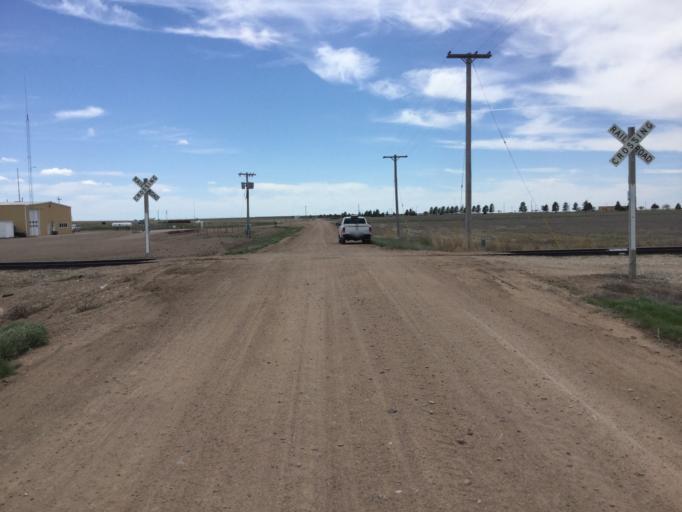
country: US
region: Kansas
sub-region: Sherman County
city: Goodland
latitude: 39.3405
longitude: -101.6887
